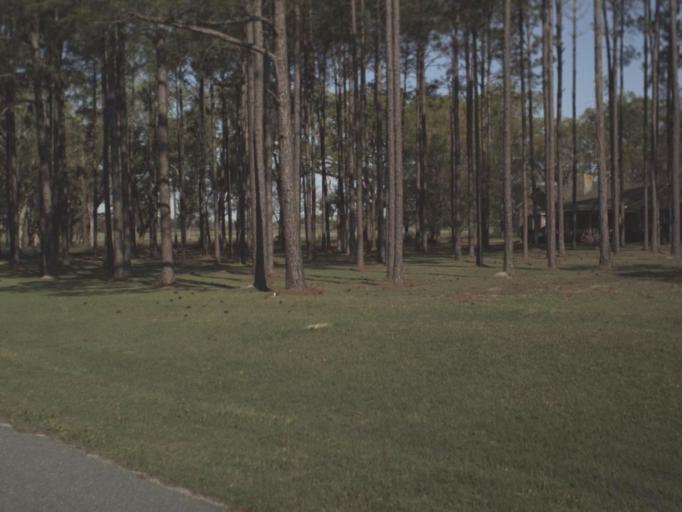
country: US
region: Florida
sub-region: Jackson County
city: Malone
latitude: 30.9590
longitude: -85.1844
